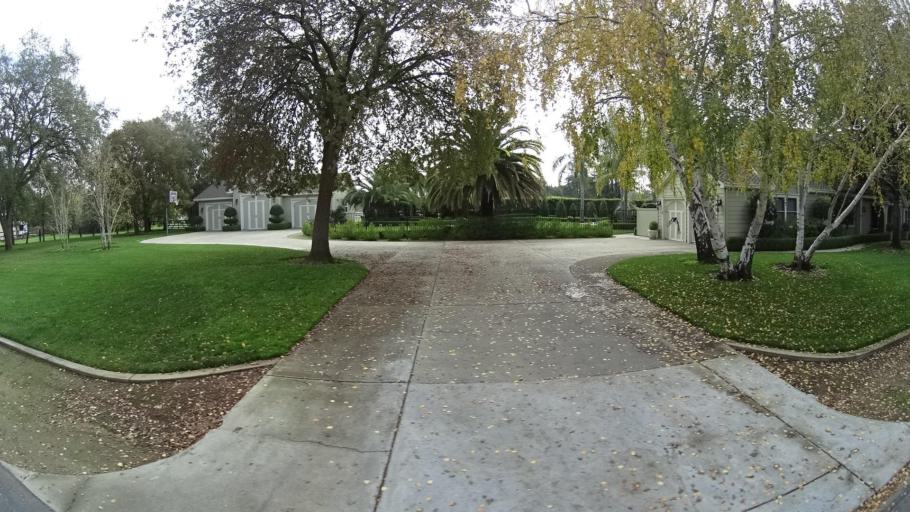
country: US
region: California
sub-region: Sacramento County
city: Vineyard
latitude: 38.4331
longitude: -121.3266
